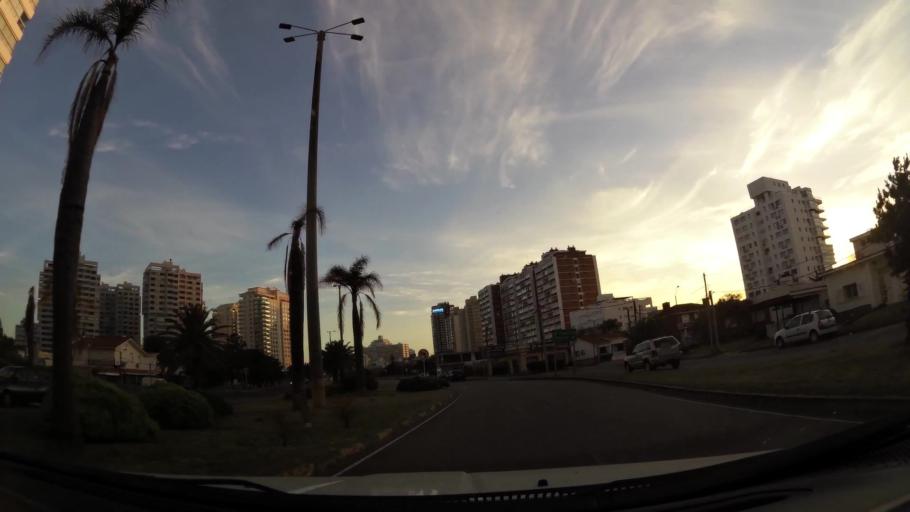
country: UY
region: Maldonado
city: Punta del Este
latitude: -34.9533
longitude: -54.9385
